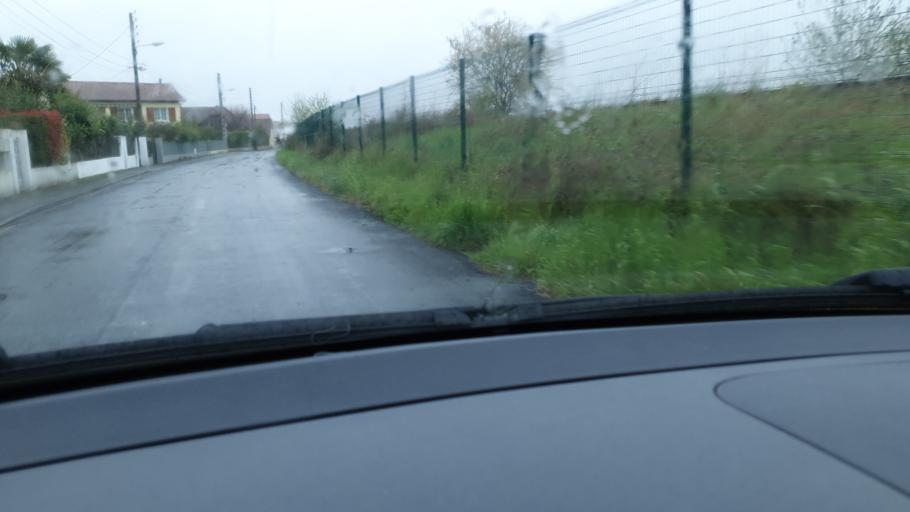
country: FR
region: Midi-Pyrenees
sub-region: Departement des Hautes-Pyrenees
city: Tarbes
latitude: 43.2465
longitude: 0.0529
